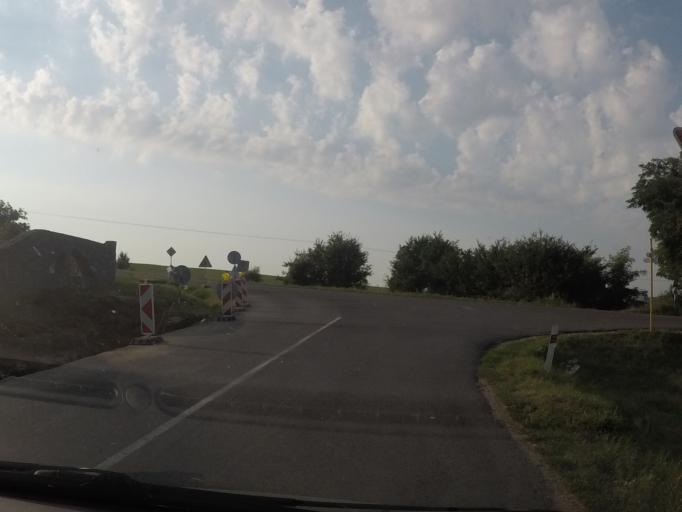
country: SK
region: Nitriansky
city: Zlate Moravce
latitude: 48.3888
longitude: 18.3632
